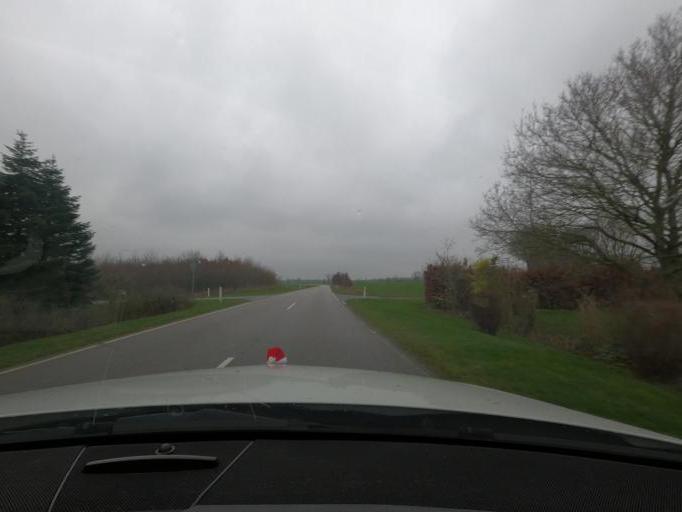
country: DK
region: South Denmark
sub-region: Haderslev Kommune
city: Starup
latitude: 55.2415
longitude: 9.6618
